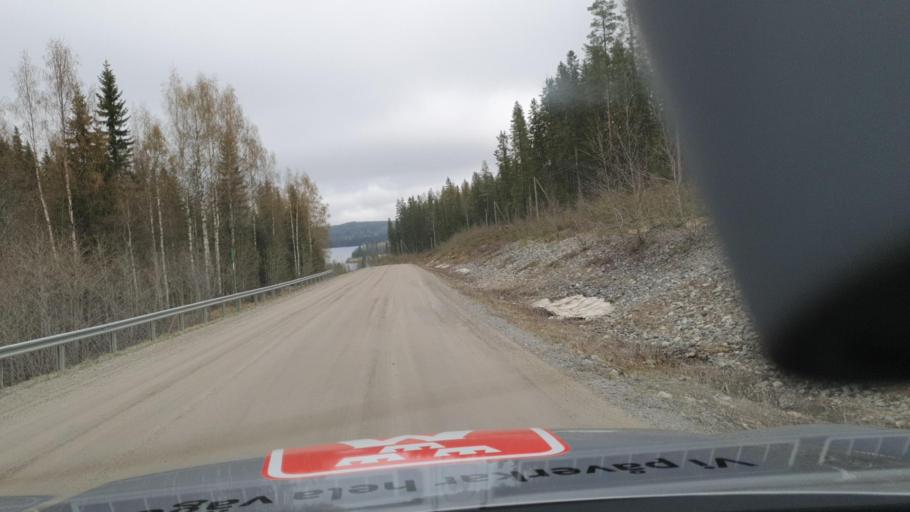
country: SE
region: Vaesternorrland
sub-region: OErnskoeldsviks Kommun
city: Husum
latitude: 63.6265
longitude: 19.0496
